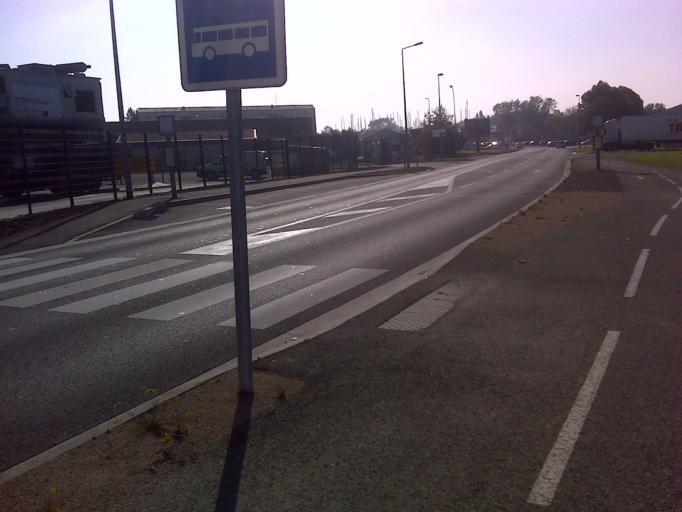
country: FR
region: Poitou-Charentes
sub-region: Departement de la Charente-Maritime
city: Rochefort
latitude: 45.9472
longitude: -0.9566
